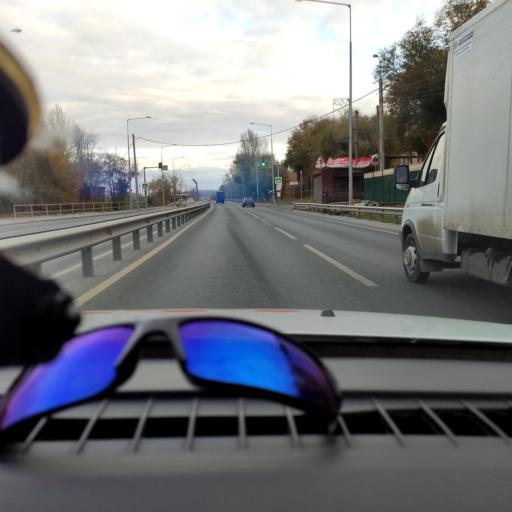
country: RU
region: Samara
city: Volzhskiy
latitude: 53.4024
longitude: 50.1476
